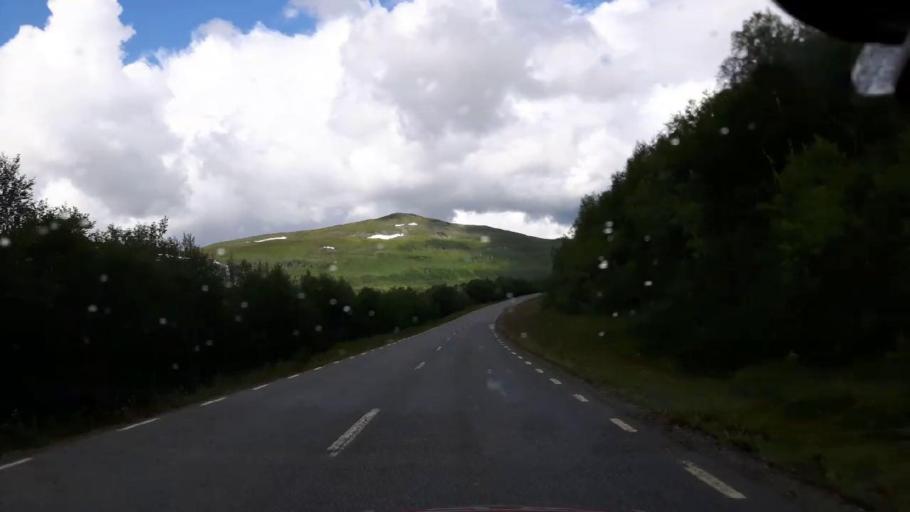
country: NO
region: Nordland
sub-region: Hattfjelldal
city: Hattfjelldal
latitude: 65.0695
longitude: 14.6606
